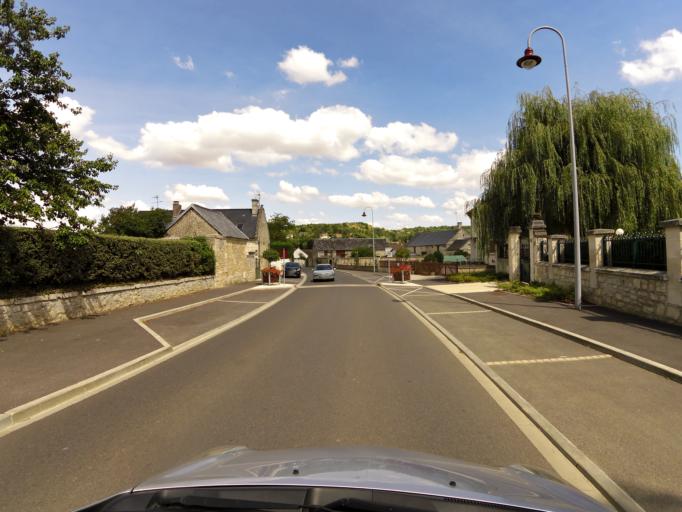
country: FR
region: Picardie
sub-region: Departement de l'Aisne
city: Courmelles
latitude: 49.3463
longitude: 3.3130
